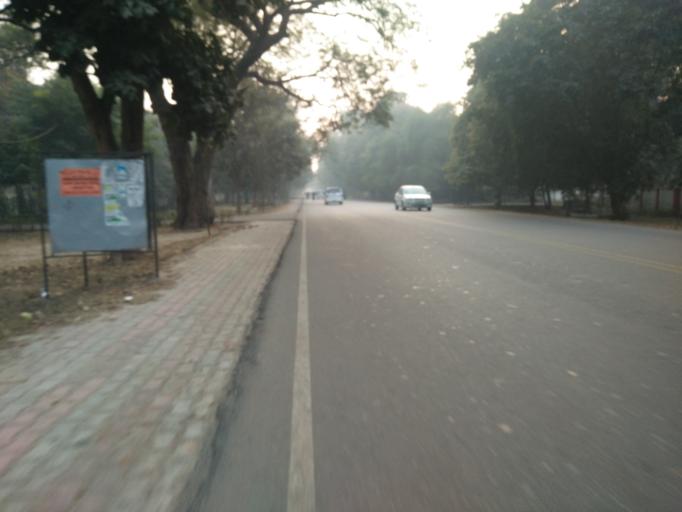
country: IN
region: Uttar Pradesh
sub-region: Lucknow District
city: Lucknow
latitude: 26.8131
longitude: 80.9437
